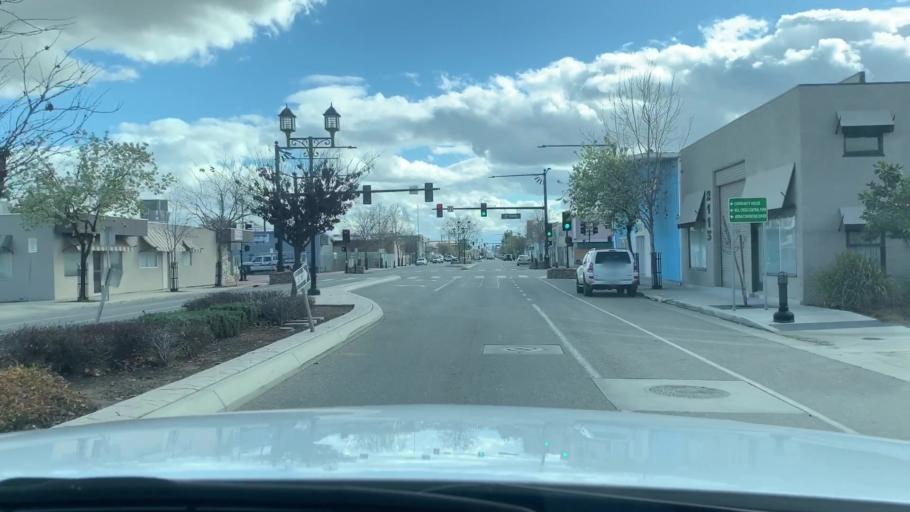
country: US
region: California
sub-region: Kern County
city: Bakersfield
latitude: 35.3786
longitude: -119.0107
